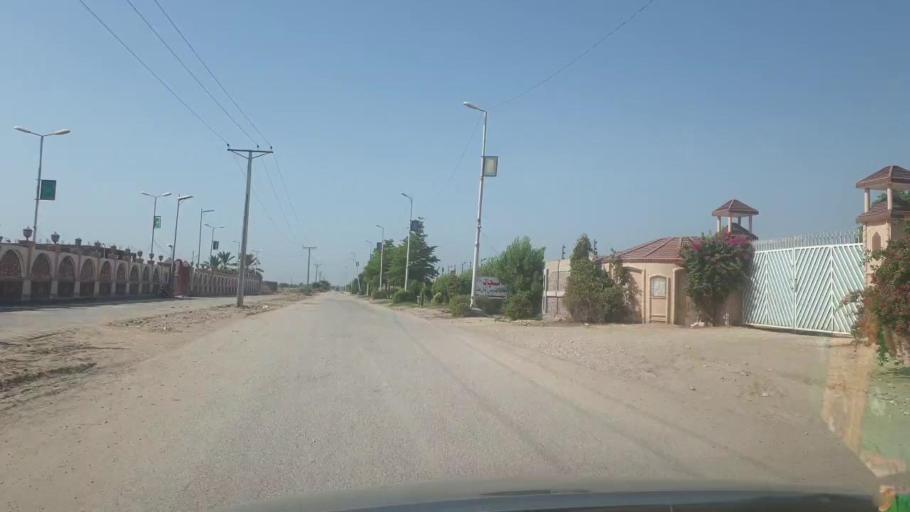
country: PK
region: Sindh
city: Rohri
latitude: 27.5223
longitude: 69.0365
